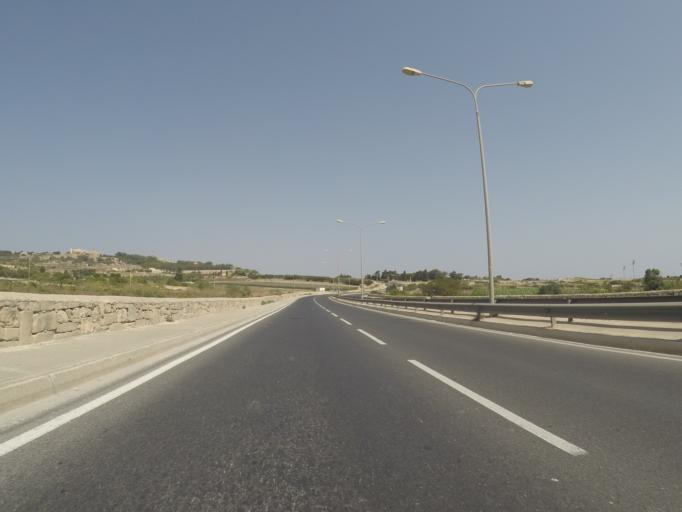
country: MT
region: L-Imdina
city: Imdina
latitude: 35.8868
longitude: 14.4106
